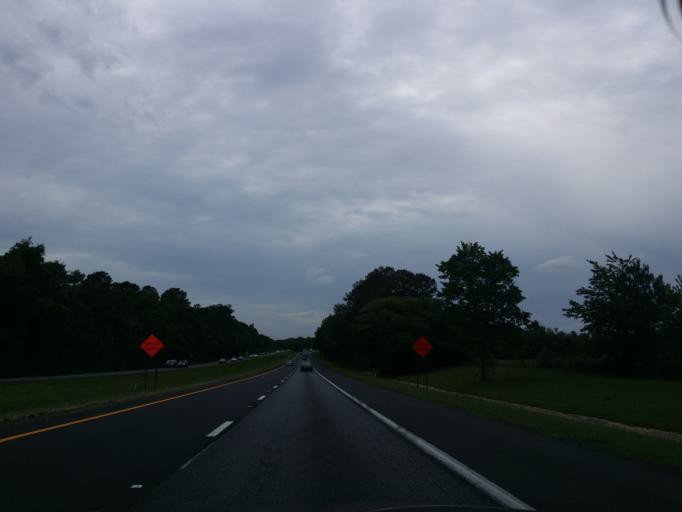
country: US
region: Florida
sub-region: Madison County
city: Madison
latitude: 30.4327
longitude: -83.5448
